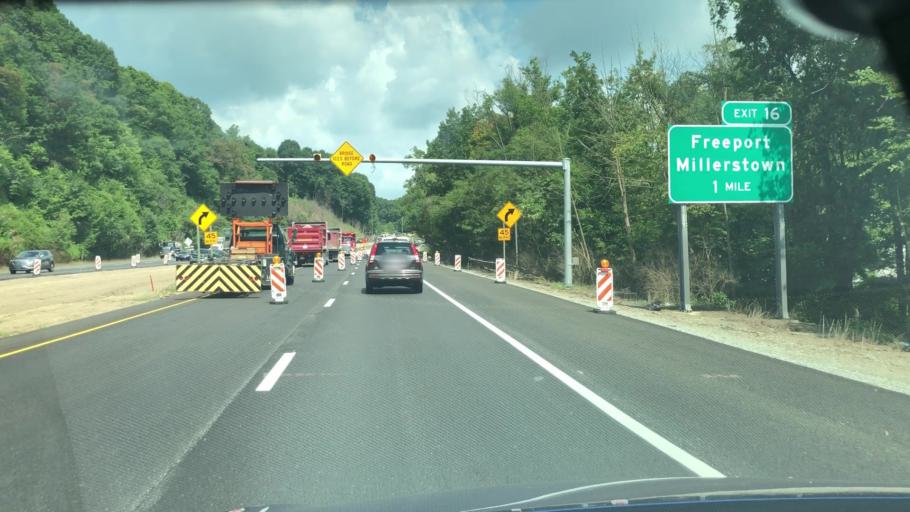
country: US
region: Pennsylvania
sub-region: Armstrong County
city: Freeport
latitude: 40.6503
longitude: -79.7234
